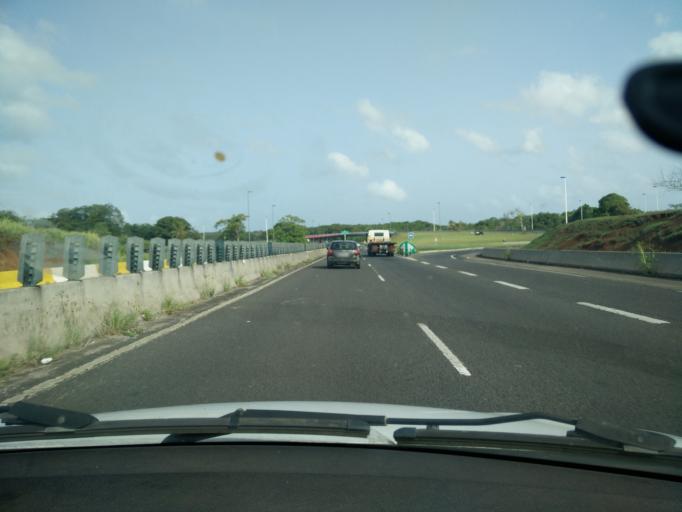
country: GP
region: Guadeloupe
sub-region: Guadeloupe
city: Les Abymes
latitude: 16.2737
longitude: -61.5177
